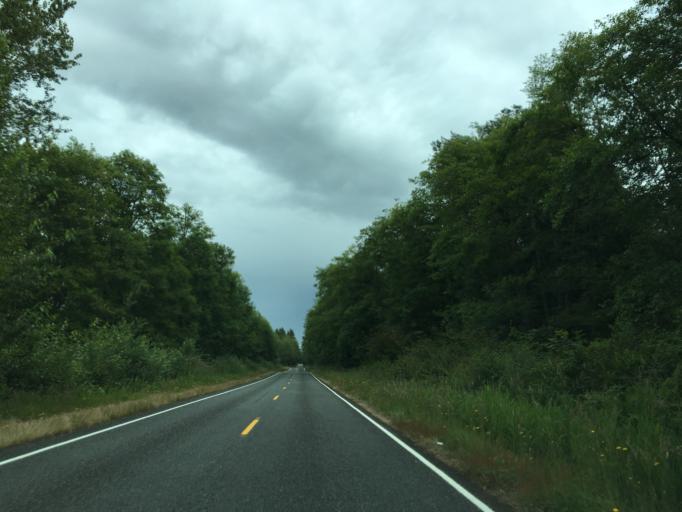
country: US
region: Washington
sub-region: Whatcom County
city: Birch Bay
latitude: 48.9432
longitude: -122.7423
